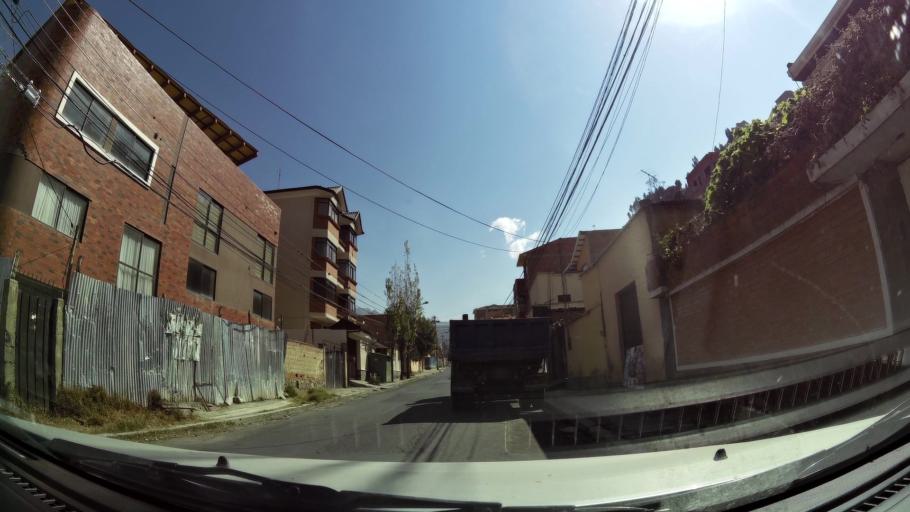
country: BO
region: La Paz
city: La Paz
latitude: -16.5195
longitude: -68.0857
